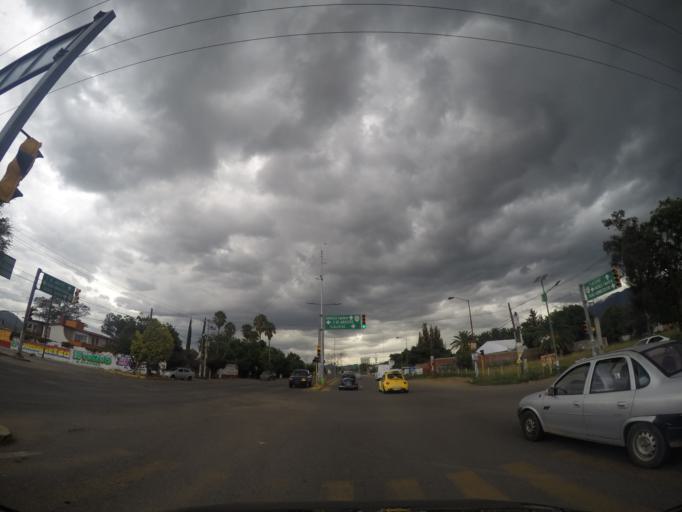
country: MX
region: Oaxaca
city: Tlalixtac de Cabrera
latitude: 17.0582
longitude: -96.6581
